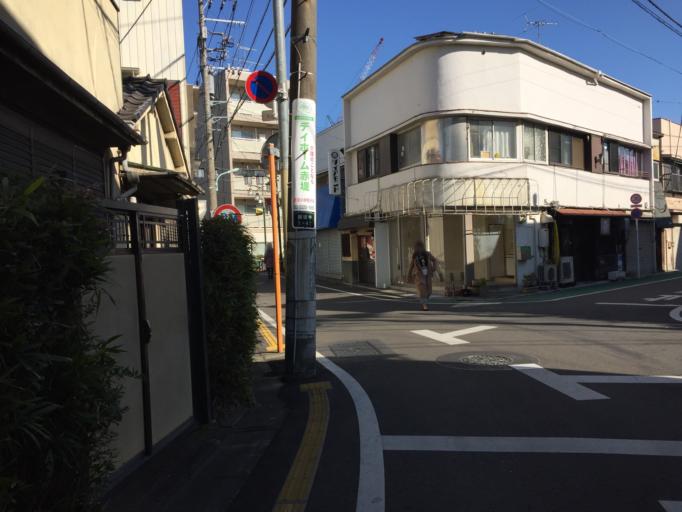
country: JP
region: Tokyo
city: Tokyo
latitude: 35.6556
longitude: 139.6485
